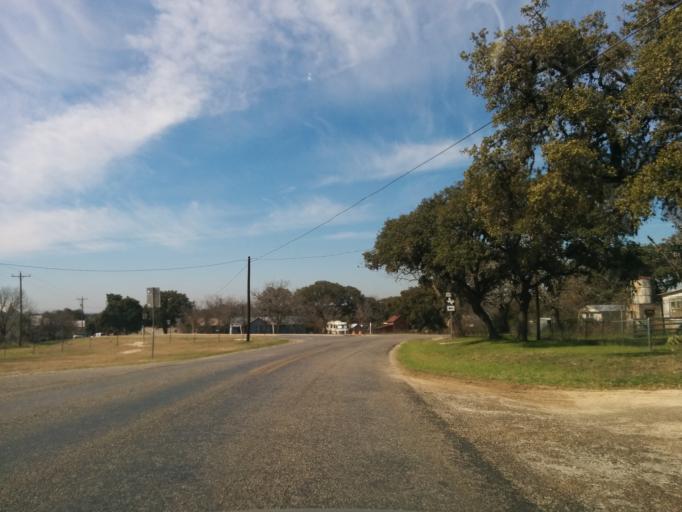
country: US
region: Texas
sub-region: Blanco County
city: Blanco
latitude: 29.9690
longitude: -98.5222
